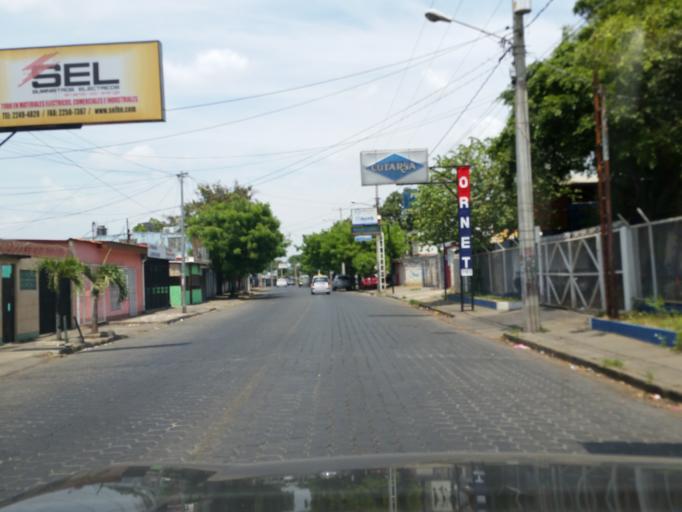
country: NI
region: Managua
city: Managua
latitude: 12.1418
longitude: -86.2467
